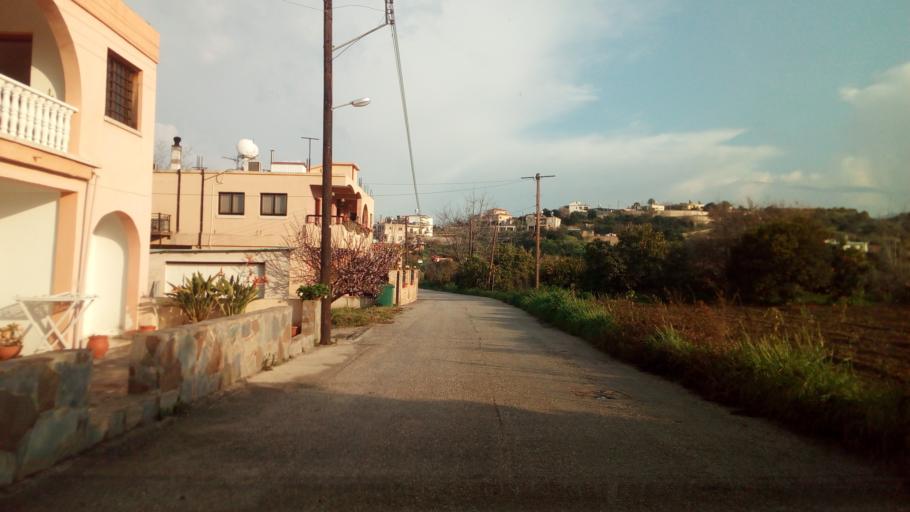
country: CY
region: Lefkosia
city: Kato Pyrgos
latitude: 35.1812
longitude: 32.6774
